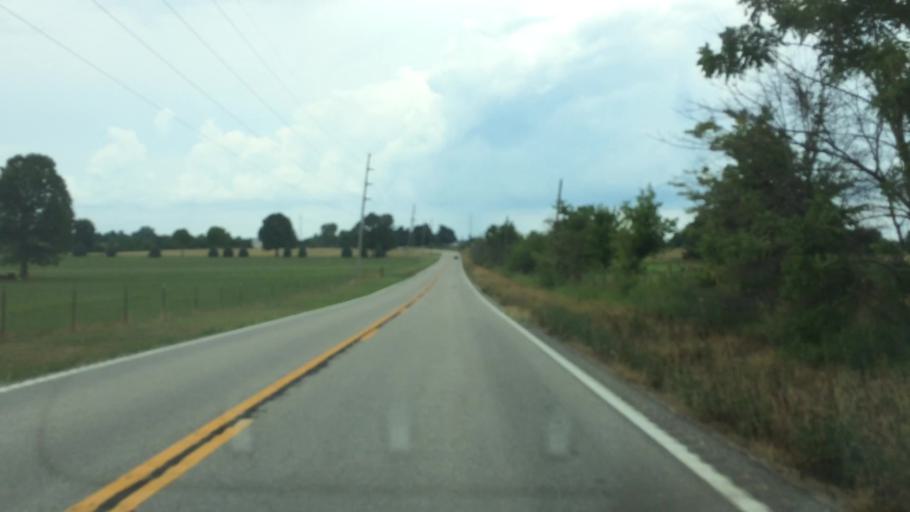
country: US
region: Missouri
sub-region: Greene County
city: Strafford
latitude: 37.2482
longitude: -93.1353
